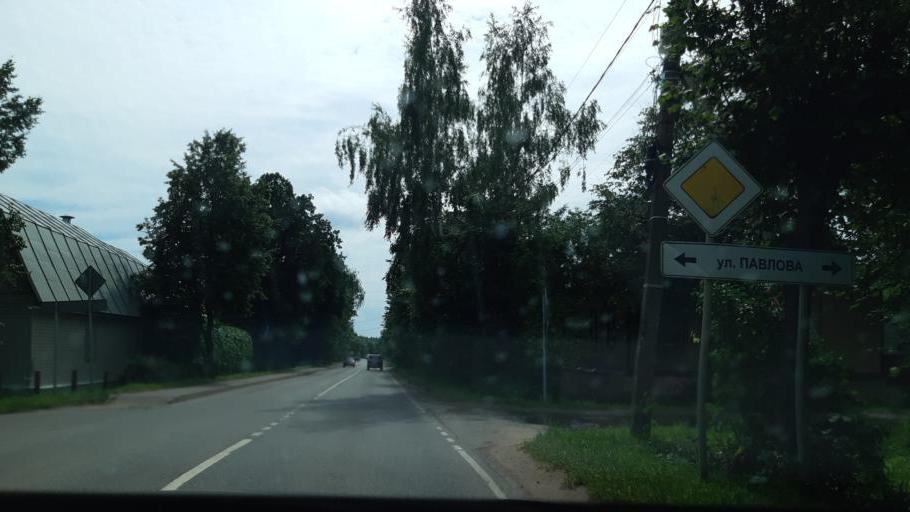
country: RU
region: Moskovskaya
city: Vereya
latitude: 55.3432
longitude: 36.1755
